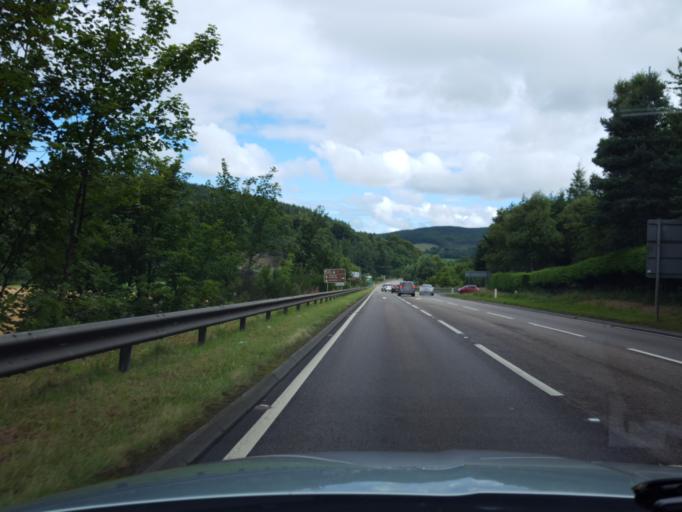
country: GB
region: Scotland
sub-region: Moray
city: Rothes
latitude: 57.4862
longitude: -3.1938
